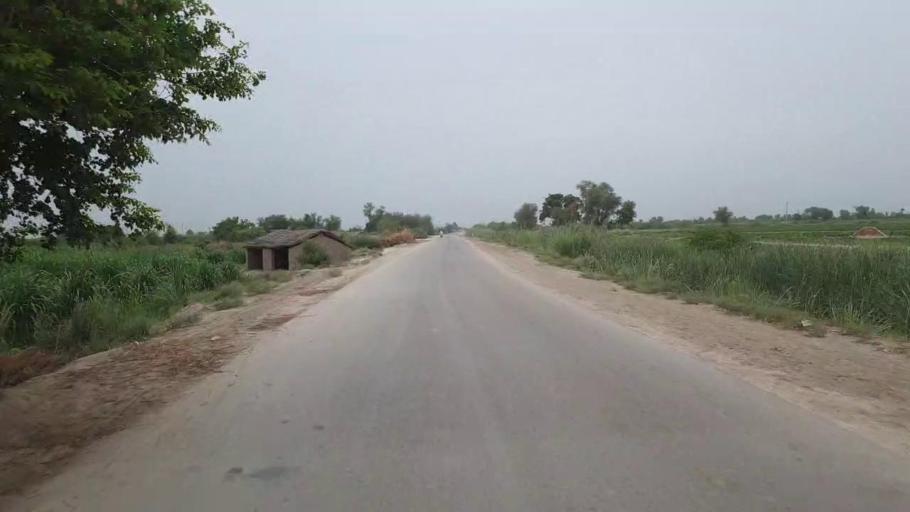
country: PK
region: Sindh
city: Bandhi
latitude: 26.5466
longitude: 68.2184
